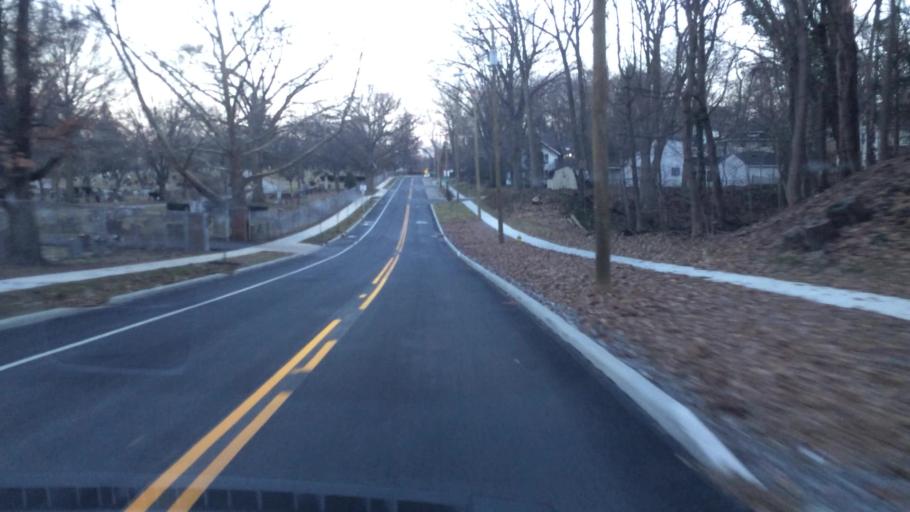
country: US
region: Ohio
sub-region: Summit County
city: Akron
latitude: 41.0986
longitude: -81.5353
